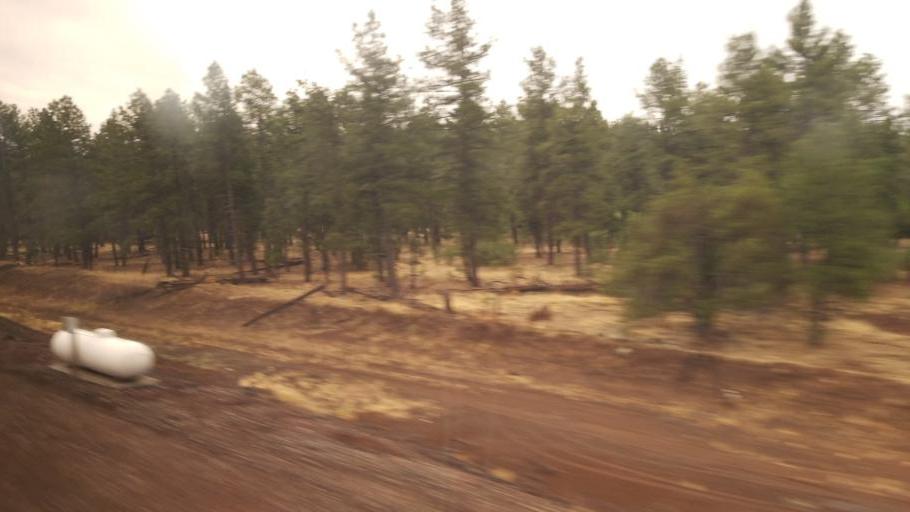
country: US
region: Arizona
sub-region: Coconino County
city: Parks
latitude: 35.2539
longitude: -111.9319
